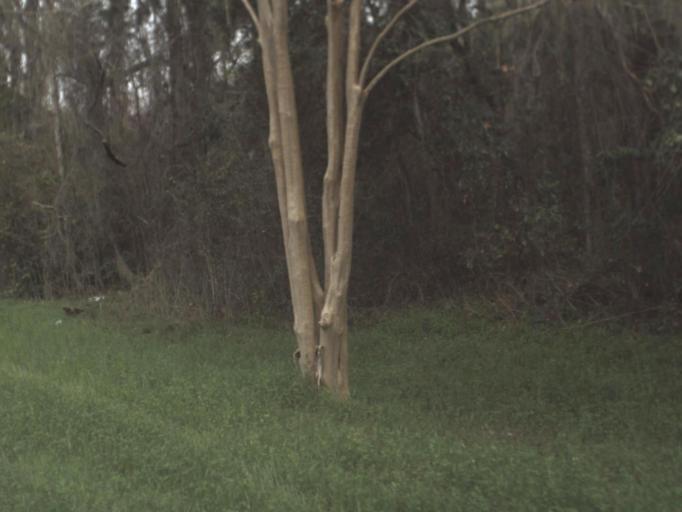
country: US
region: Florida
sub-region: Jefferson County
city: Monticello
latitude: 30.5288
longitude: -83.9883
